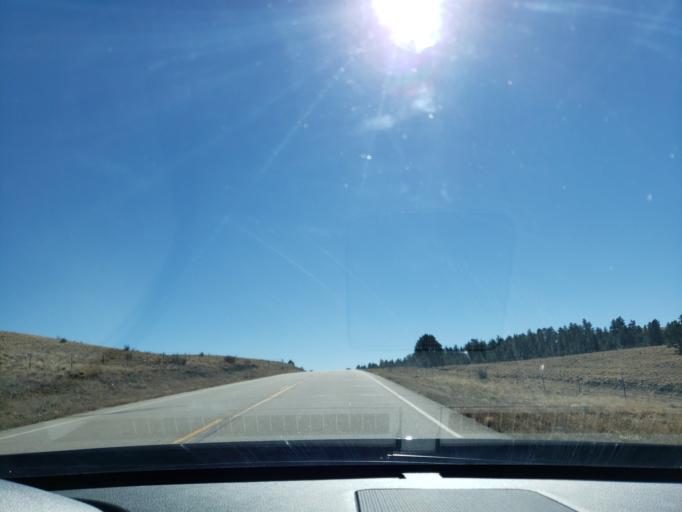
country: US
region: Colorado
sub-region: Park County
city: Fairplay
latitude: 38.9113
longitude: -105.7020
